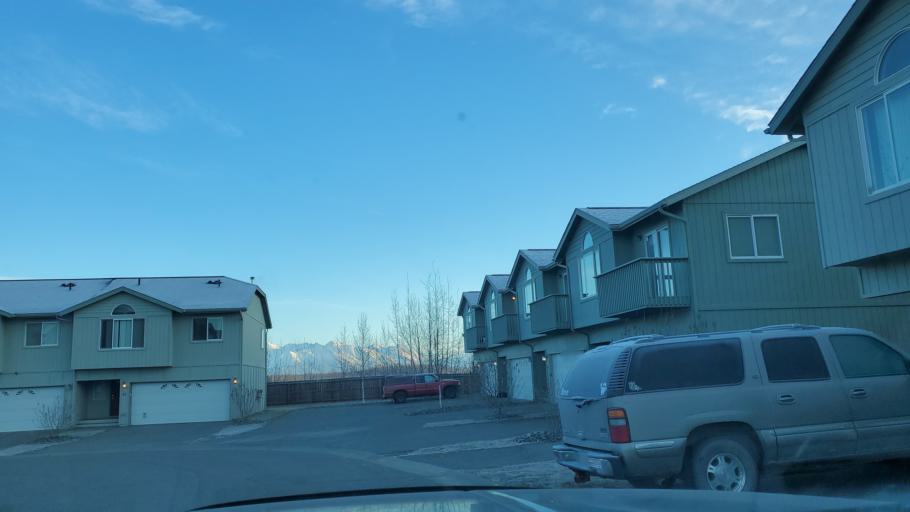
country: US
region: Alaska
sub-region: Matanuska-Susitna Borough
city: Wasilla
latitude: 61.5789
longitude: -149.4268
